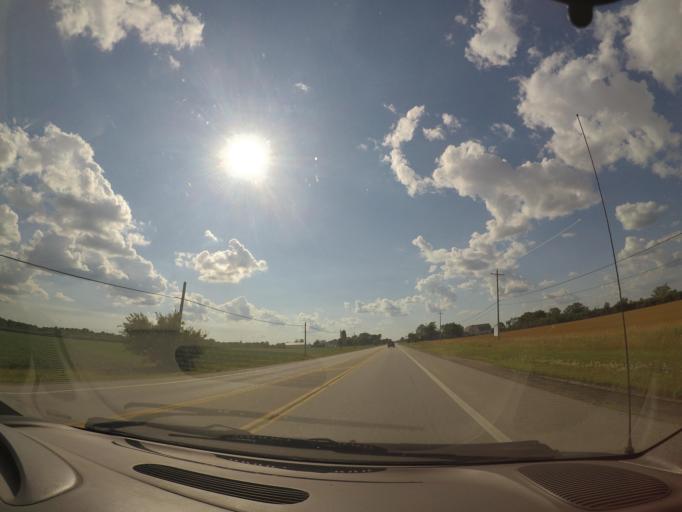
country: US
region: Ohio
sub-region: Wood County
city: Perrysburg
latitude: 41.5364
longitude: -83.5700
